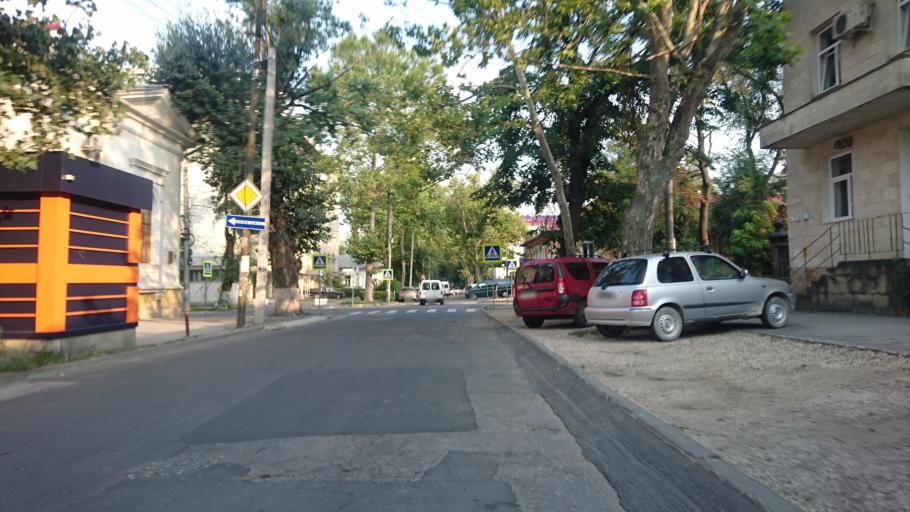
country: MD
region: Chisinau
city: Chisinau
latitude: 47.0291
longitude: 28.8199
